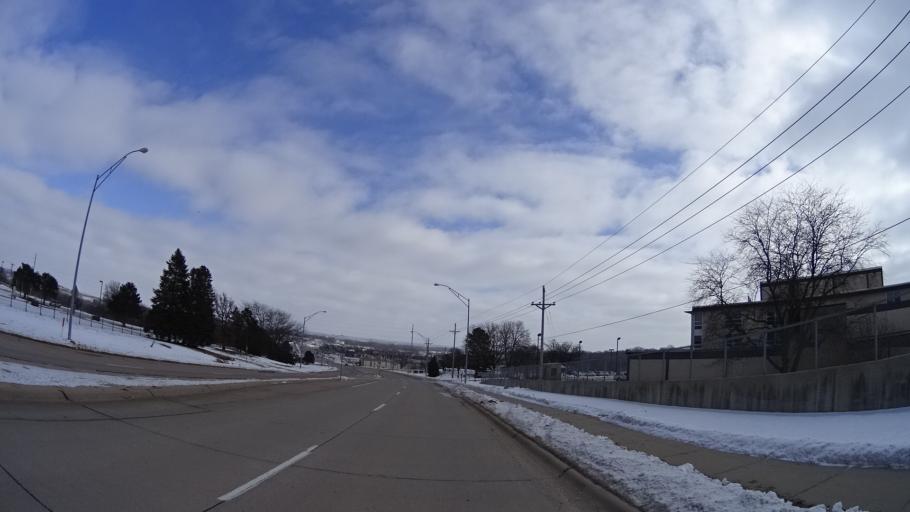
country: US
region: Nebraska
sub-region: Sarpy County
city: Offutt Air Force Base
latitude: 41.1191
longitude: -95.9500
